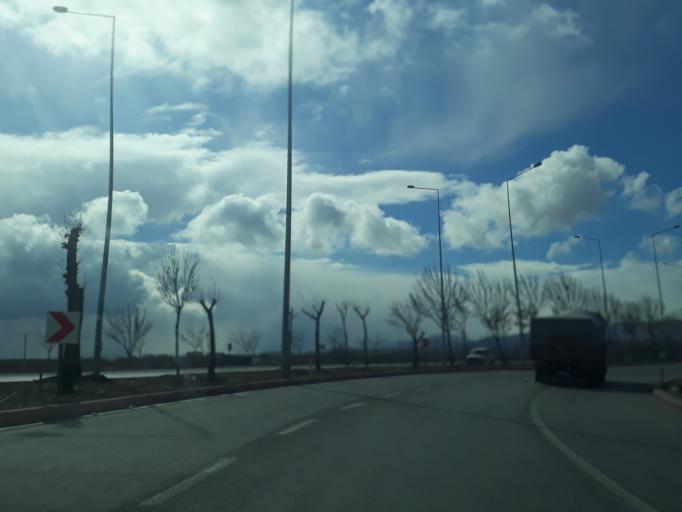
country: TR
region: Konya
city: Asagipinarbasi
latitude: 38.0050
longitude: 32.5523
